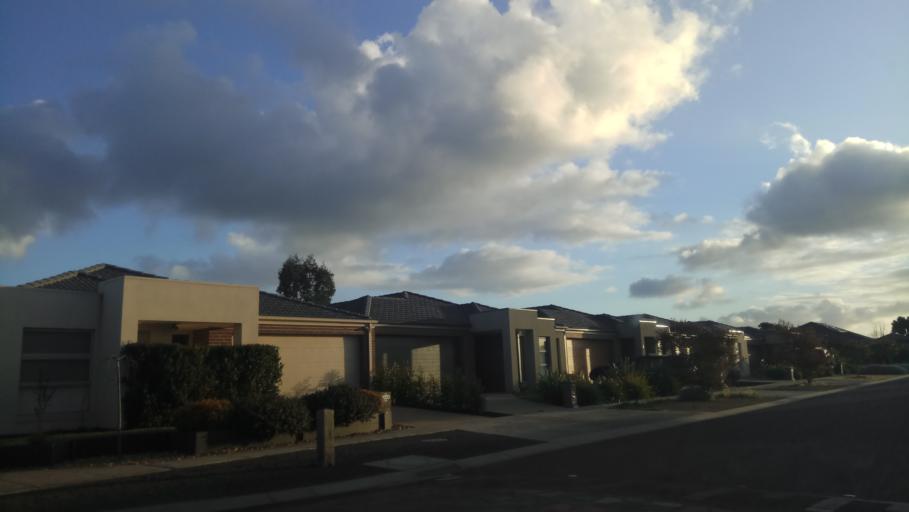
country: AU
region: Victoria
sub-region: Wyndham
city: Point Cook
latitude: -37.9105
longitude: 144.7771
